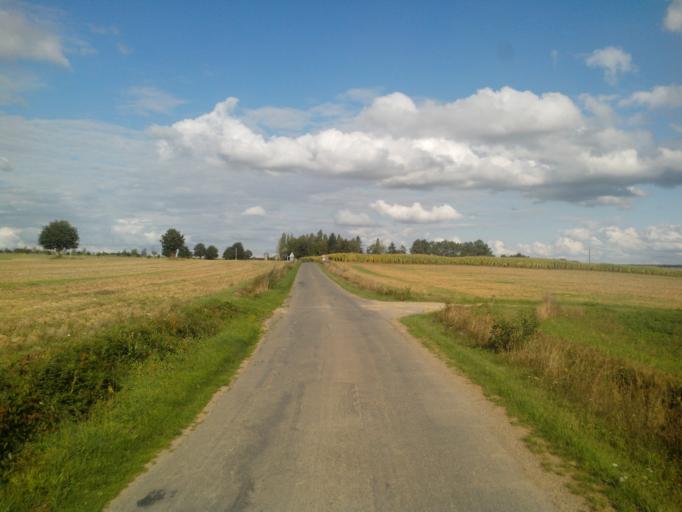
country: FR
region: Brittany
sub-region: Departement d'Ille-et-Vilaine
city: Boisgervilly
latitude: 48.1096
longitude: -2.0988
